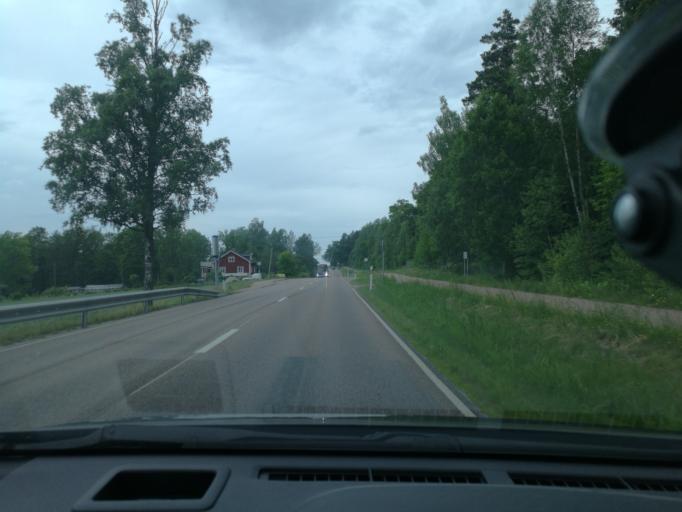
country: SE
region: Vaestmanland
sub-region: Vasteras
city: Skultuna
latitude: 59.6726
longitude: 16.4724
